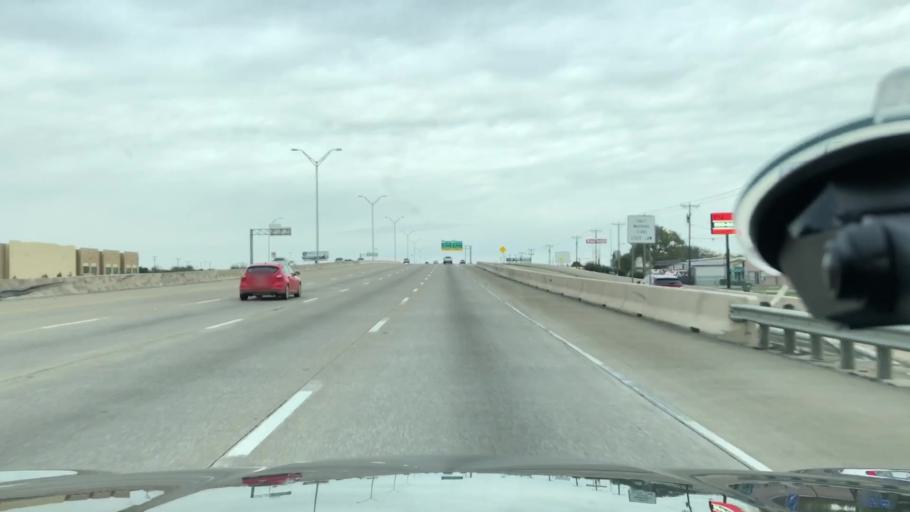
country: US
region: Texas
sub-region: Dallas County
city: DeSoto
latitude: 32.6295
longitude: -96.8230
